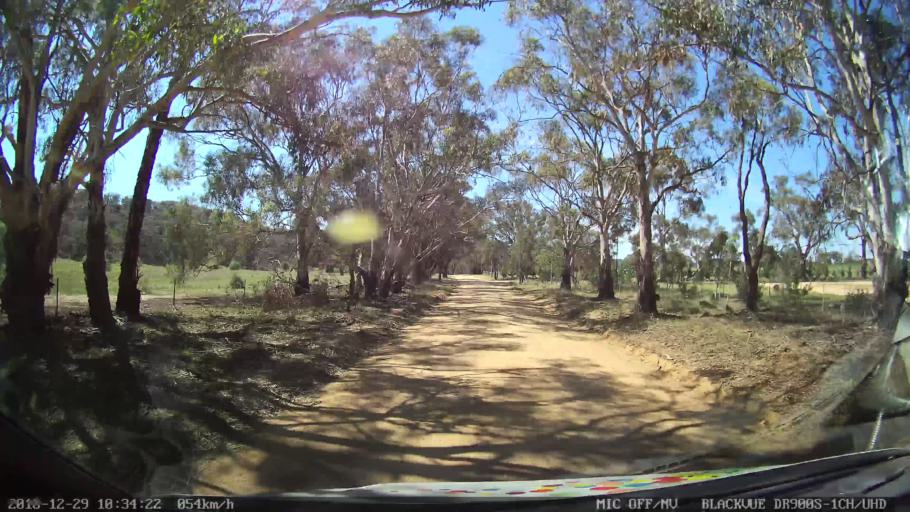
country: AU
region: New South Wales
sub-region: Yass Valley
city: Gundaroo
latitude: -34.9862
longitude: 149.4776
